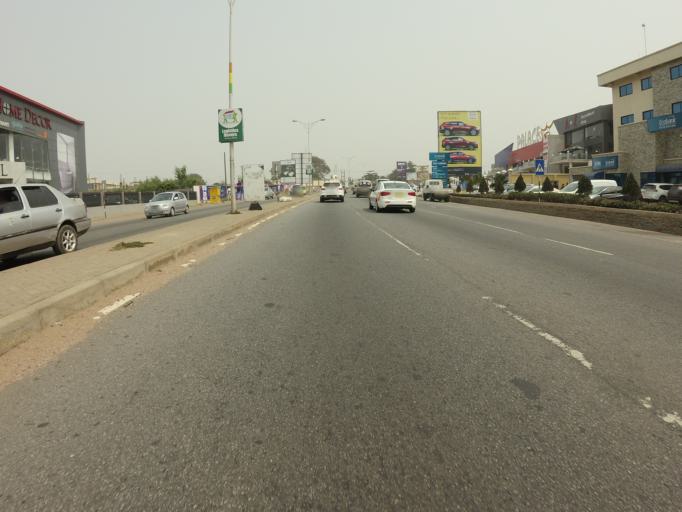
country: GH
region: Greater Accra
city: Medina Estates
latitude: 5.6267
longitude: -0.1548
